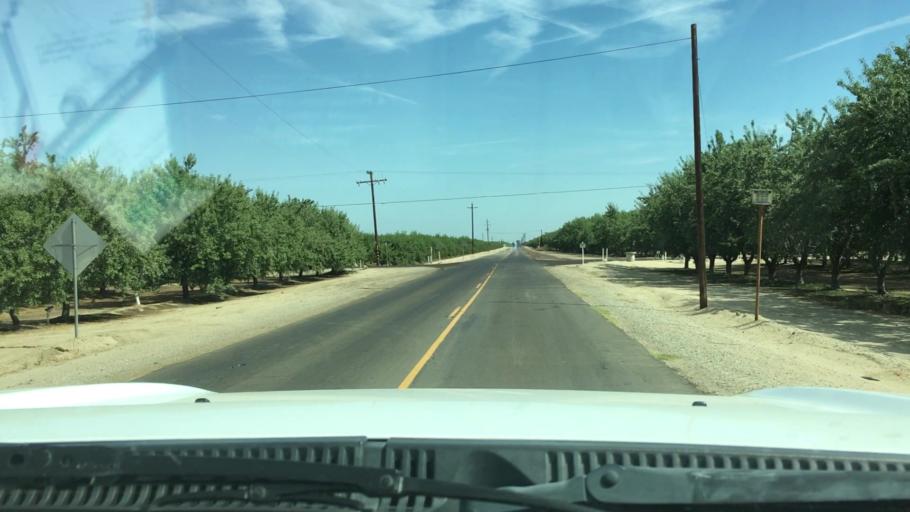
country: US
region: California
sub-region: Kern County
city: Wasco
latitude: 35.5283
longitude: -119.3498
